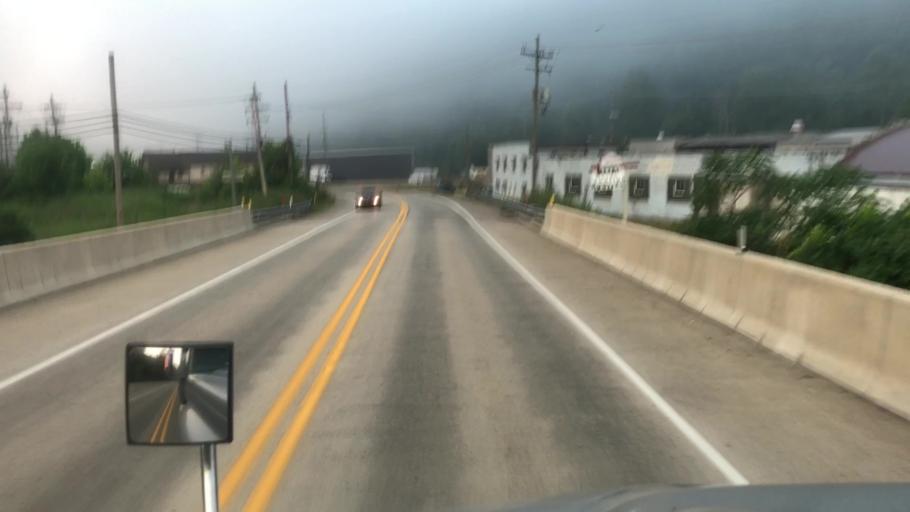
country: US
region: Pennsylvania
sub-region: Venango County
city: Hasson Heights
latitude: 41.4599
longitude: -79.6898
